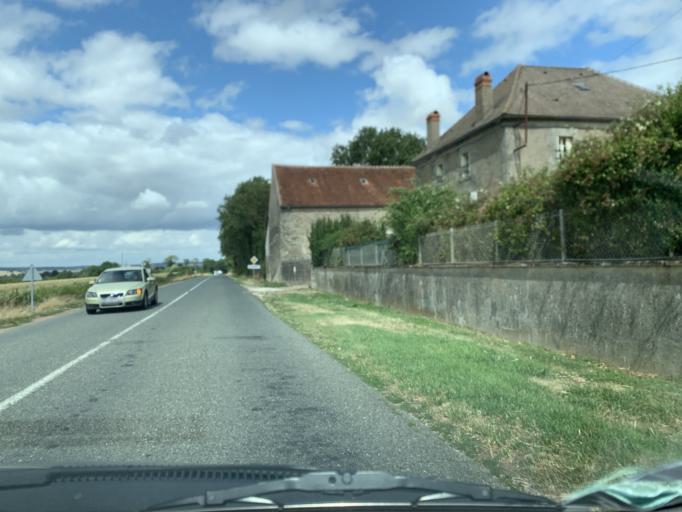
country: FR
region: Bourgogne
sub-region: Departement de la Nievre
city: Varzy
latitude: 47.3895
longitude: 3.4441
